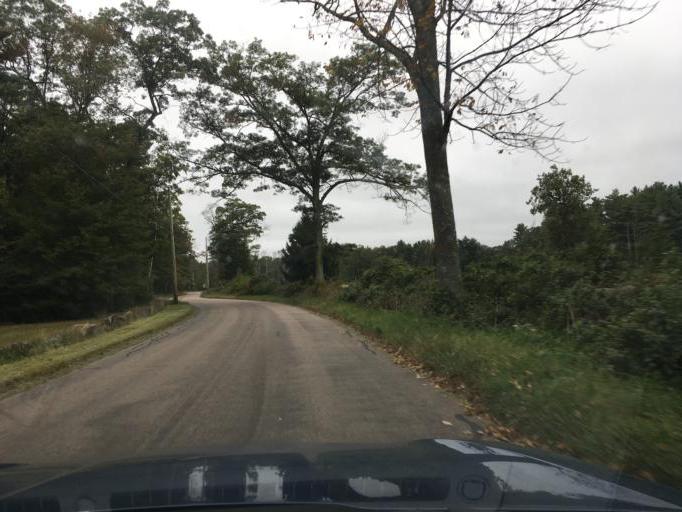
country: US
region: Rhode Island
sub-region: Washington County
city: Exeter
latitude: 41.5923
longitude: -71.5627
